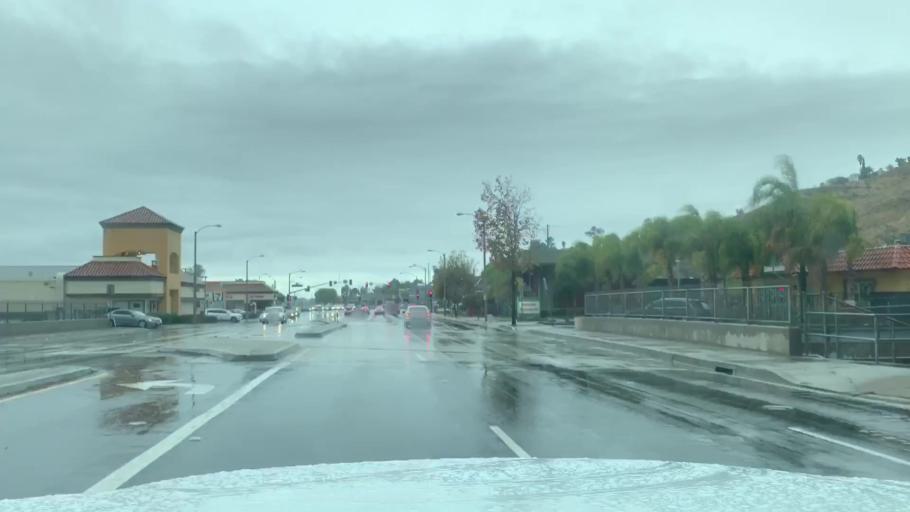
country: US
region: California
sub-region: Los Angeles County
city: Santa Clarita
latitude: 34.4165
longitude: -118.4536
